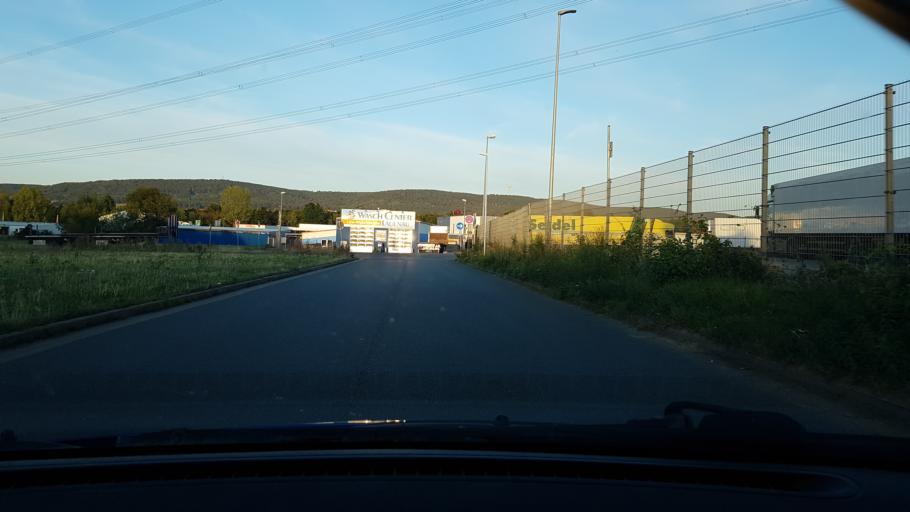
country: DE
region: Lower Saxony
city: Pohle
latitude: 52.2757
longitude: 9.3513
